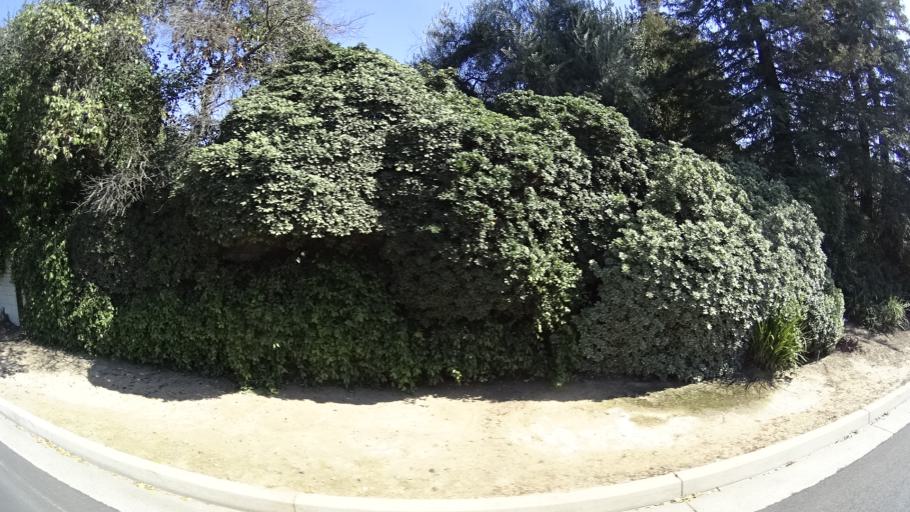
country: US
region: California
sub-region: Fresno County
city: Fresno
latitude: 36.8060
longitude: -119.8085
